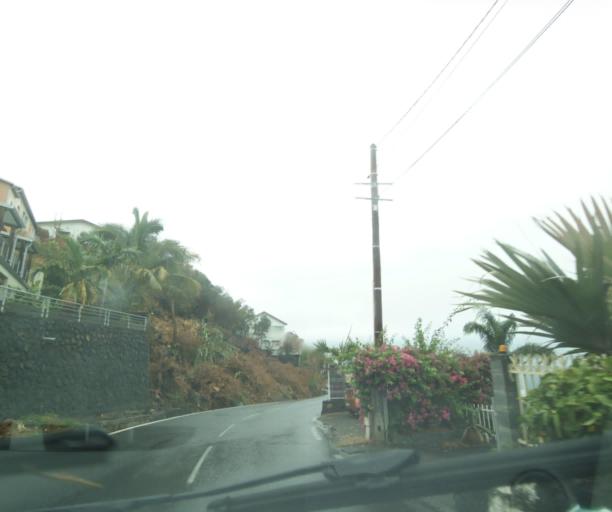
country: RE
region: Reunion
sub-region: Reunion
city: Saint-Paul
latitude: -21.0192
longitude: 55.2875
